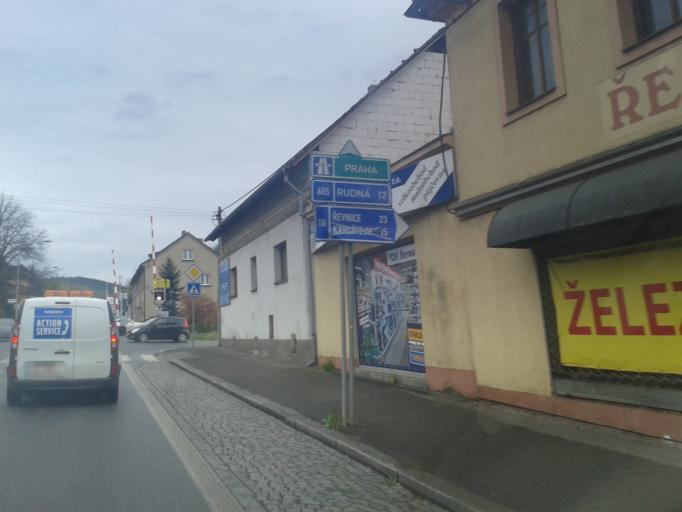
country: CZ
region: Central Bohemia
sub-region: Okres Beroun
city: Beroun
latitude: 49.9689
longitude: 14.0797
